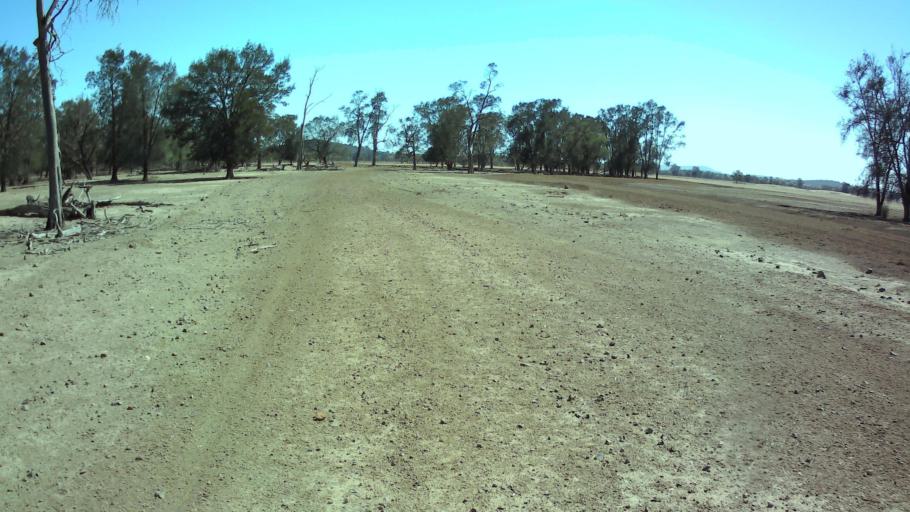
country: AU
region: New South Wales
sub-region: Bland
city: West Wyalong
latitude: -33.7582
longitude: 147.6590
